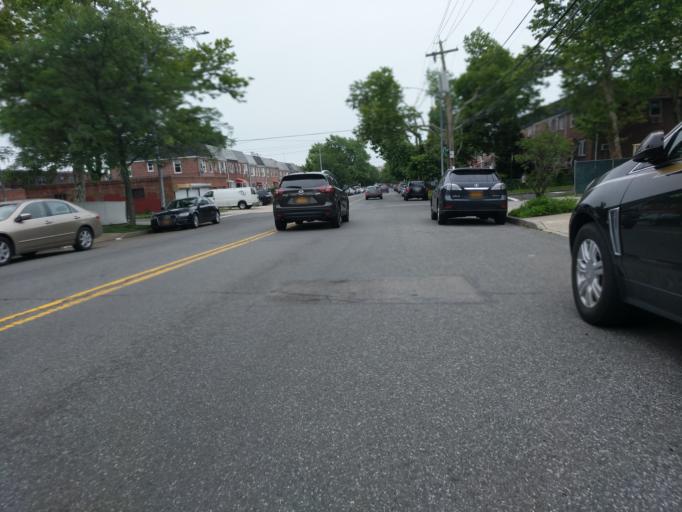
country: US
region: New York
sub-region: Queens County
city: Jamaica
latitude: 40.7447
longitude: -73.8201
